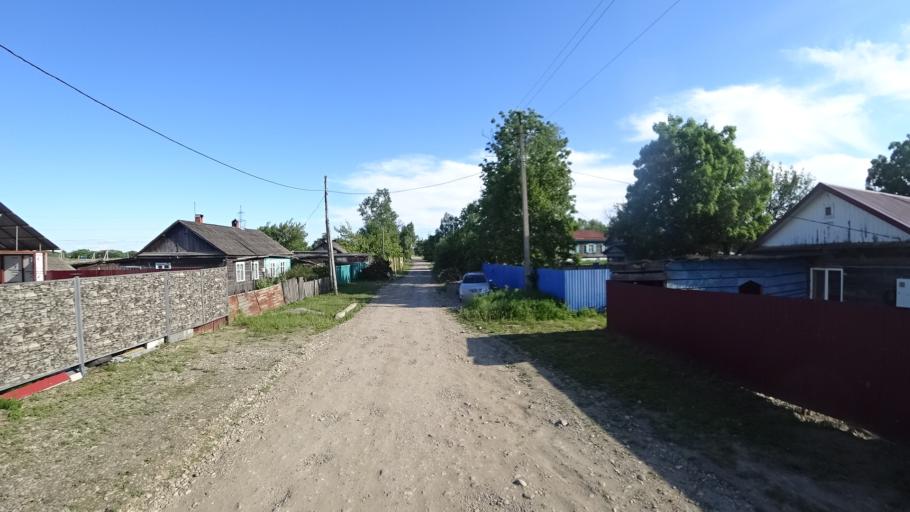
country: RU
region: Khabarovsk Krai
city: Khor
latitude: 47.8930
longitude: 134.9854
